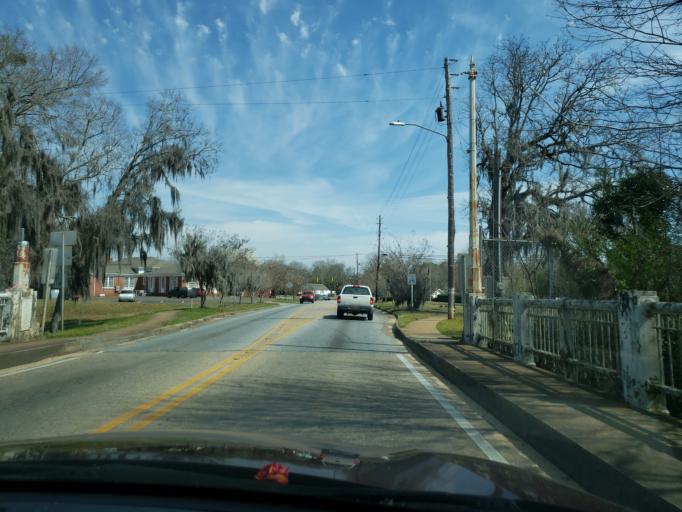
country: US
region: Alabama
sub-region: Elmore County
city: Tallassee
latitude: 32.5339
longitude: -85.8856
